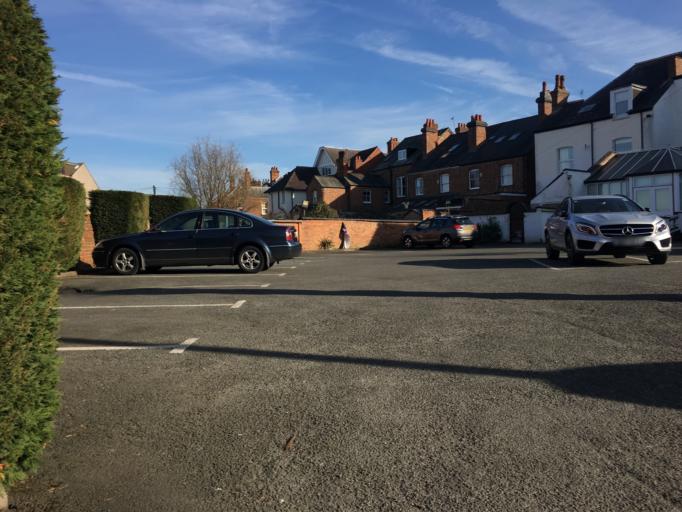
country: GB
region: England
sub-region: Warwickshire
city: Rugby
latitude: 52.3726
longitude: -1.2527
